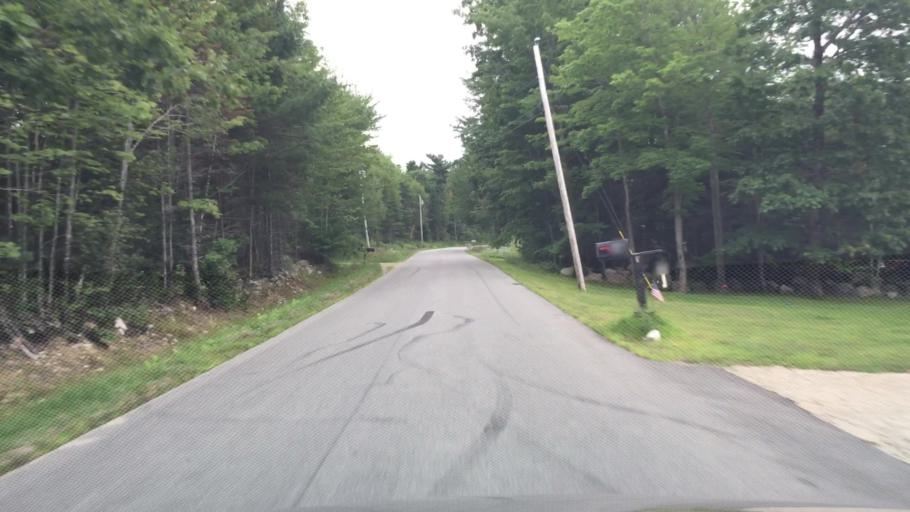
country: US
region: Maine
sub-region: Waldo County
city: Stockton Springs
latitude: 44.5159
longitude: -68.8758
